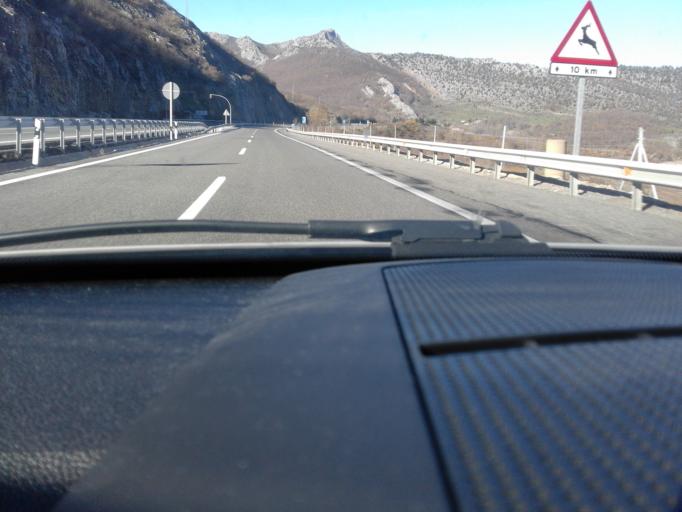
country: ES
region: Castille and Leon
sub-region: Provincia de Leon
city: Soto y Amio
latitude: 42.8626
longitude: -5.8744
